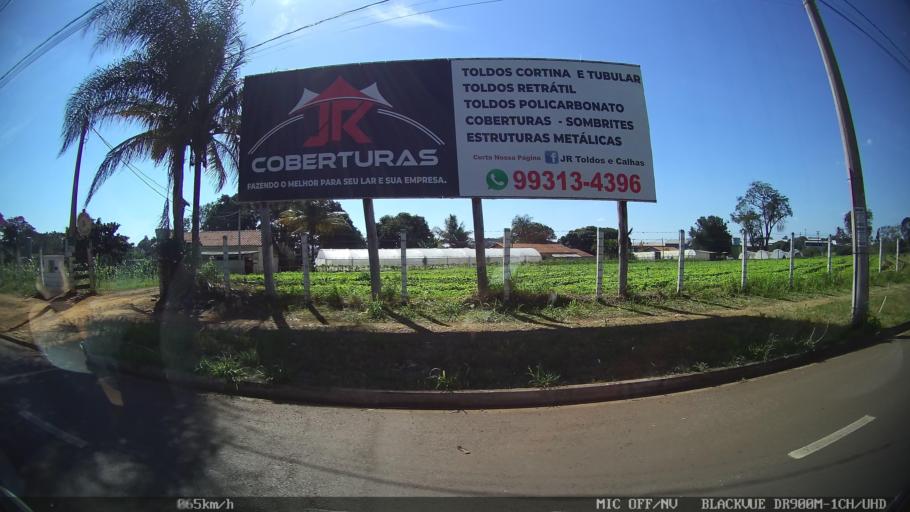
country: BR
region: Sao Paulo
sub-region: Franca
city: Franca
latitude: -20.5486
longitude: -47.4453
